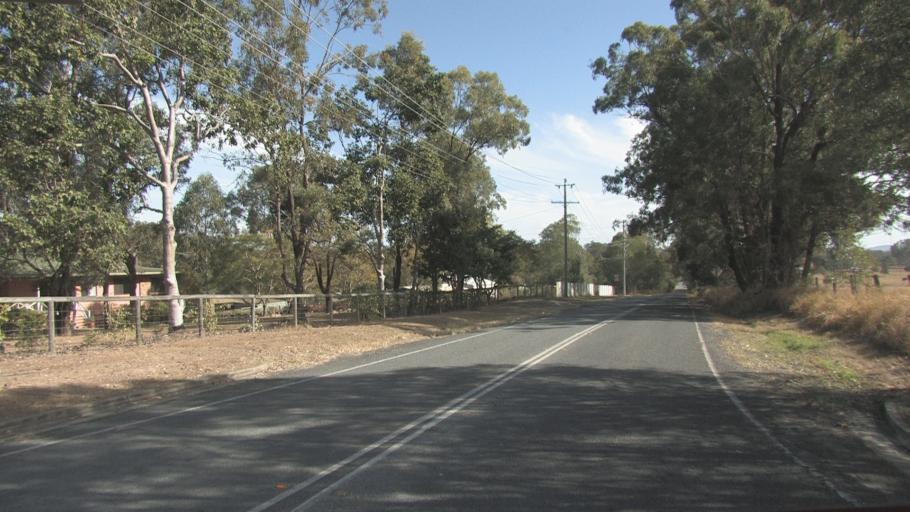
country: AU
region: Queensland
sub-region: Logan
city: Cedar Vale
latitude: -27.8678
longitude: 153.0177
